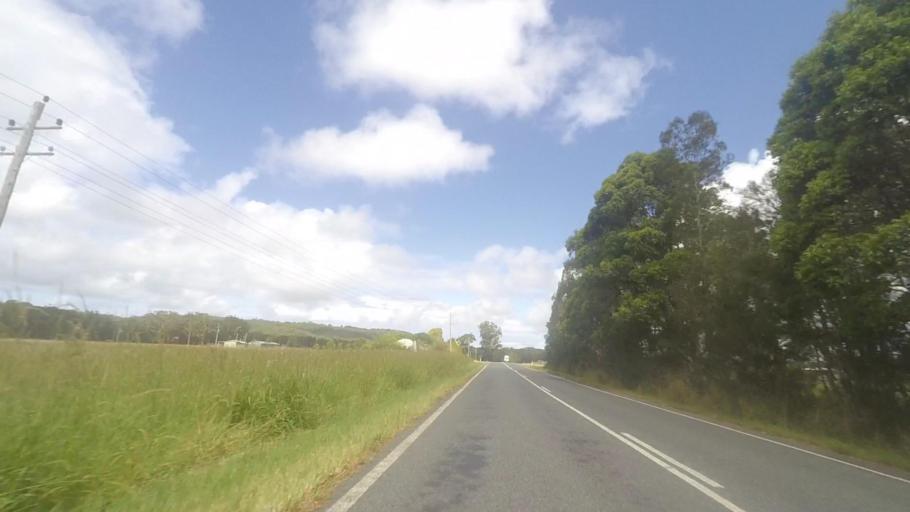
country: AU
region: New South Wales
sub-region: Great Lakes
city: Bulahdelah
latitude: -32.3863
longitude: 152.4087
